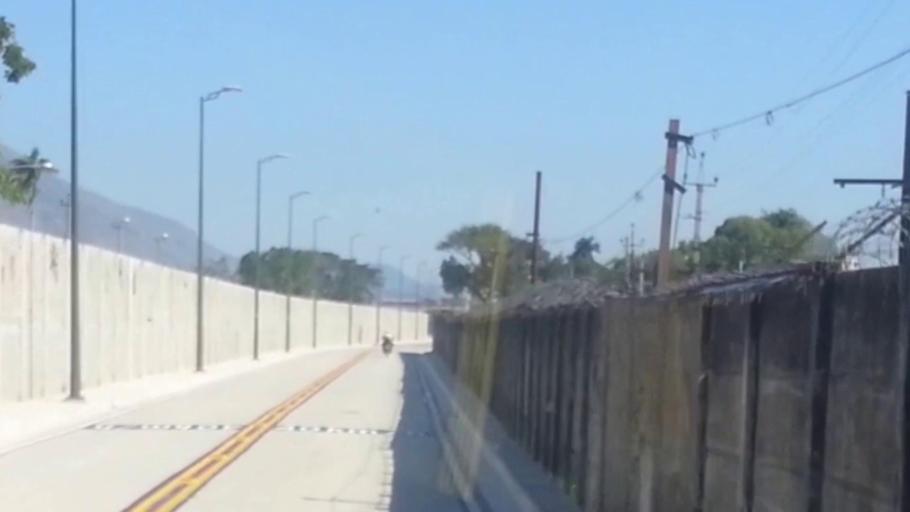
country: BR
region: Rio de Janeiro
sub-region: Nilopolis
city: Nilopolis
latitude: -22.8610
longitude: -43.3984
